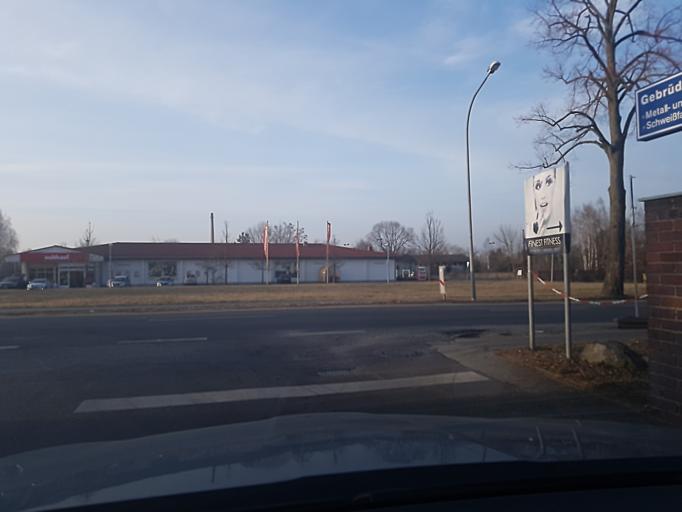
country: DE
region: Brandenburg
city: Finsterwalde
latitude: 51.6359
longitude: 13.7248
